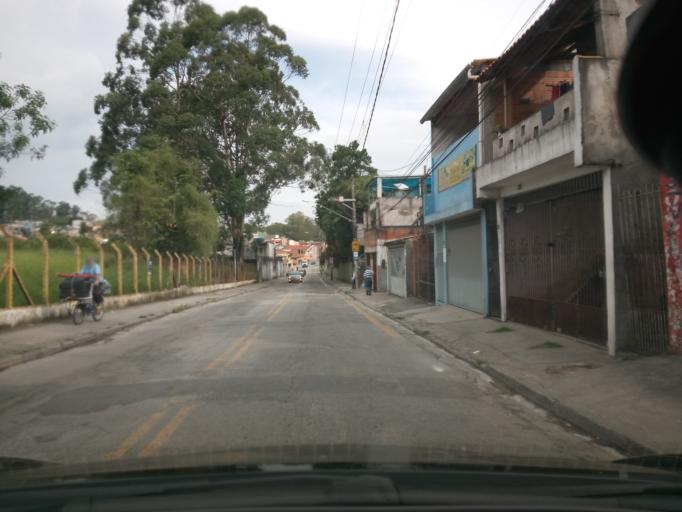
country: BR
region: Sao Paulo
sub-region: Sao Bernardo Do Campo
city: Sao Bernardo do Campo
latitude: -23.7405
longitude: -46.5961
